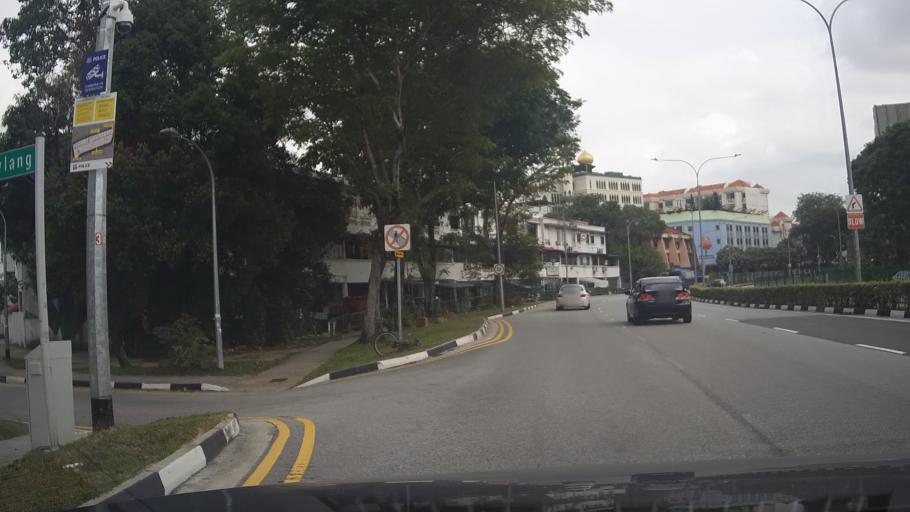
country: SG
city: Singapore
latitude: 1.3089
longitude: 103.8773
